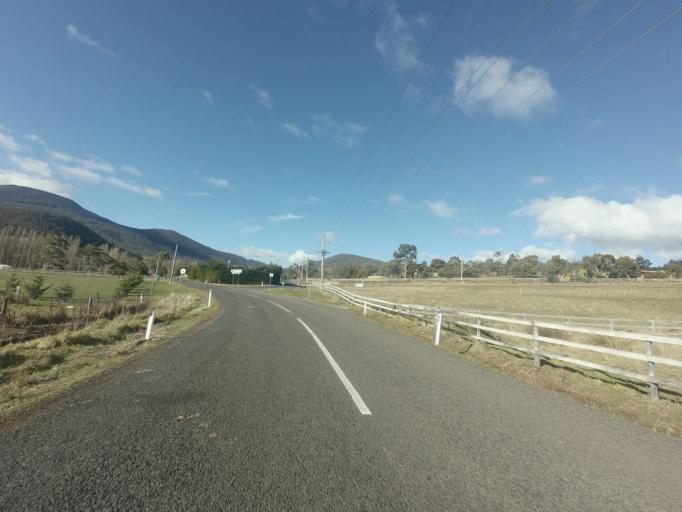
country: AU
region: Tasmania
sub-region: Derwent Valley
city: New Norfolk
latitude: -42.7989
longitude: 147.1347
